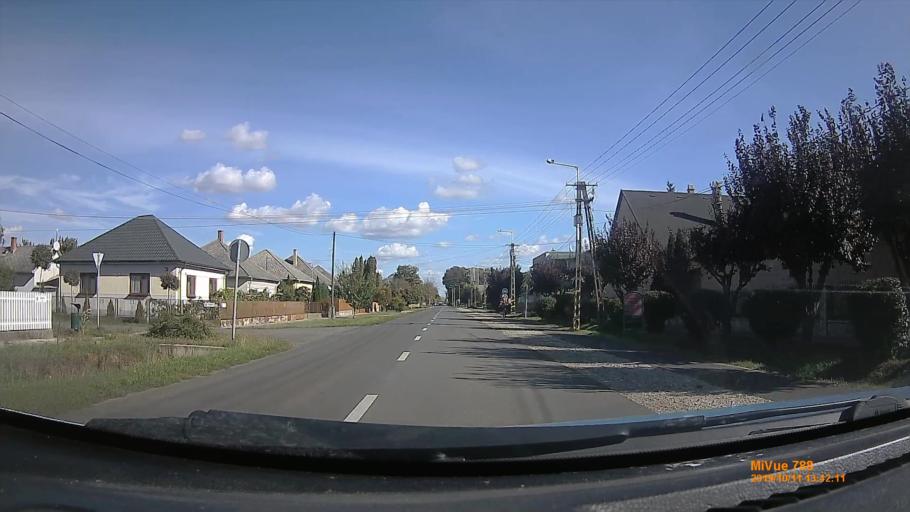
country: HU
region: Hajdu-Bihar
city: Balmazujvaros
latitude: 47.5394
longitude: 21.3413
